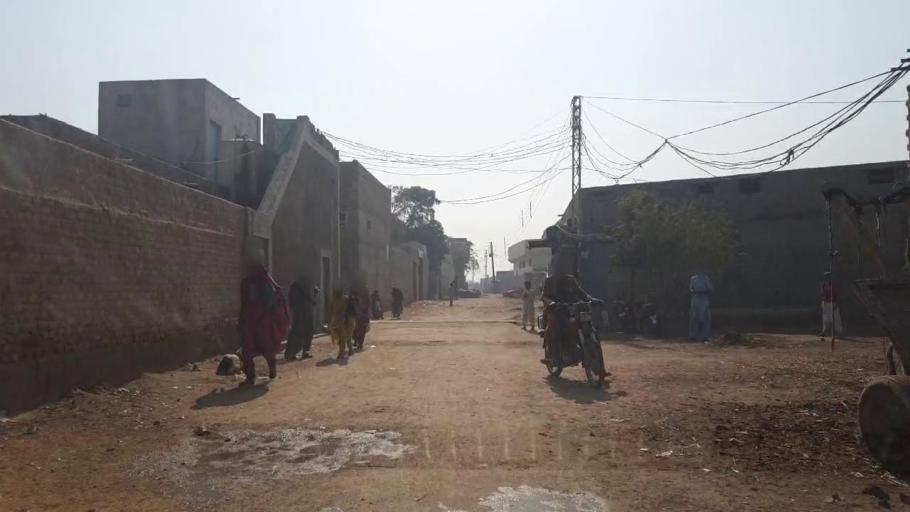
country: PK
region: Sindh
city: Tando Allahyar
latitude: 25.3625
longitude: 68.6493
